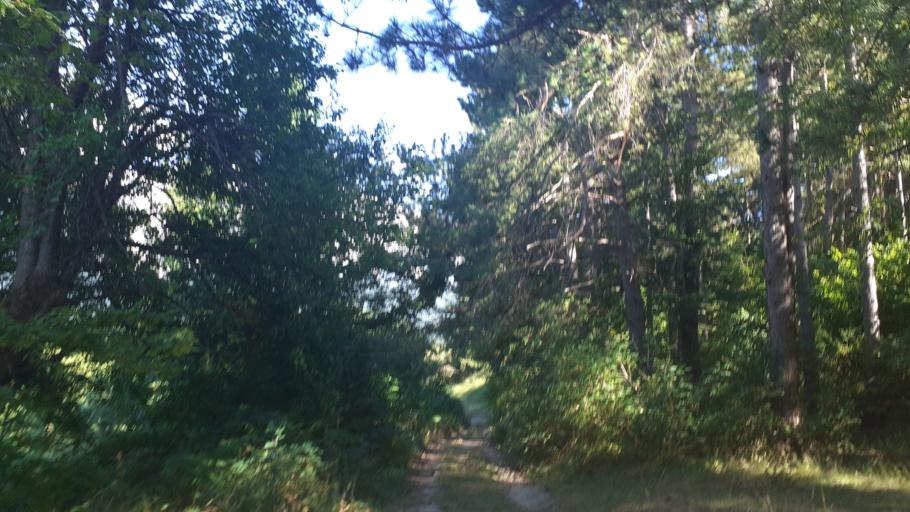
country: IT
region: Abruzzo
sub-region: Provincia di Pescara
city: Sant'Eufemia a Maiella
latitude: 42.1046
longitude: 14.0069
